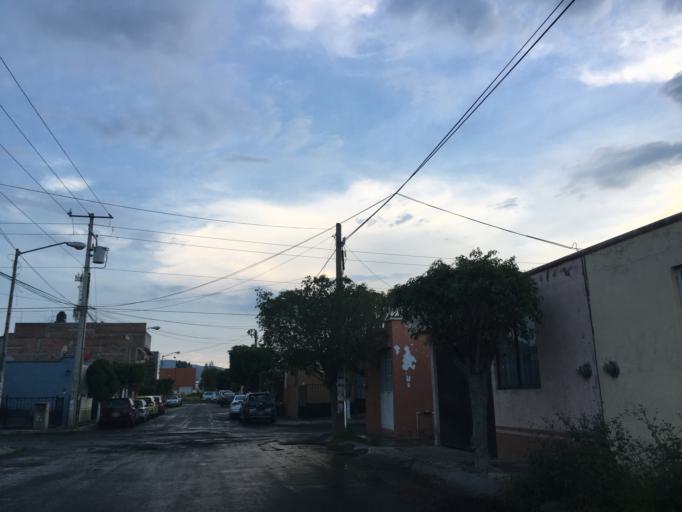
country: MX
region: Michoacan
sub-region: Morelia
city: Morelos
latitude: 19.6729
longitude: -101.2281
